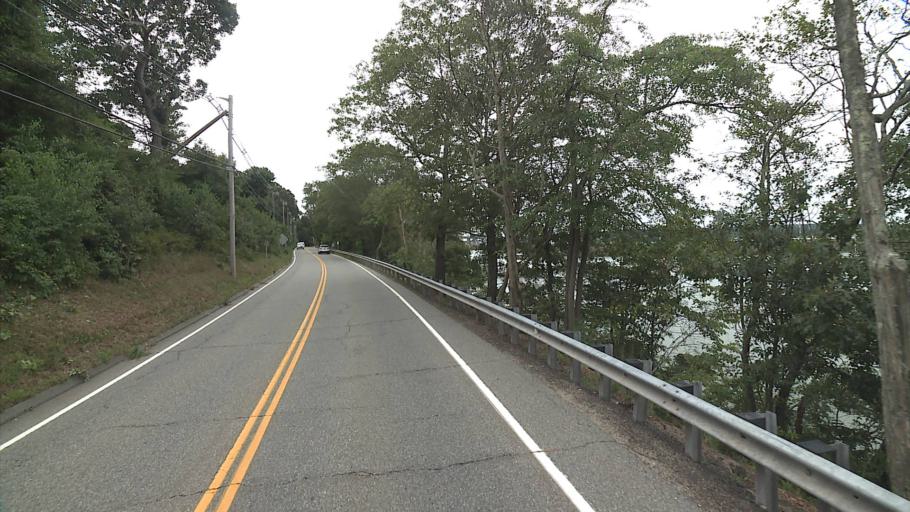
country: US
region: Connecticut
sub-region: Middlesex County
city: Old Saybrook Center
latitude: 41.3288
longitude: -72.3405
